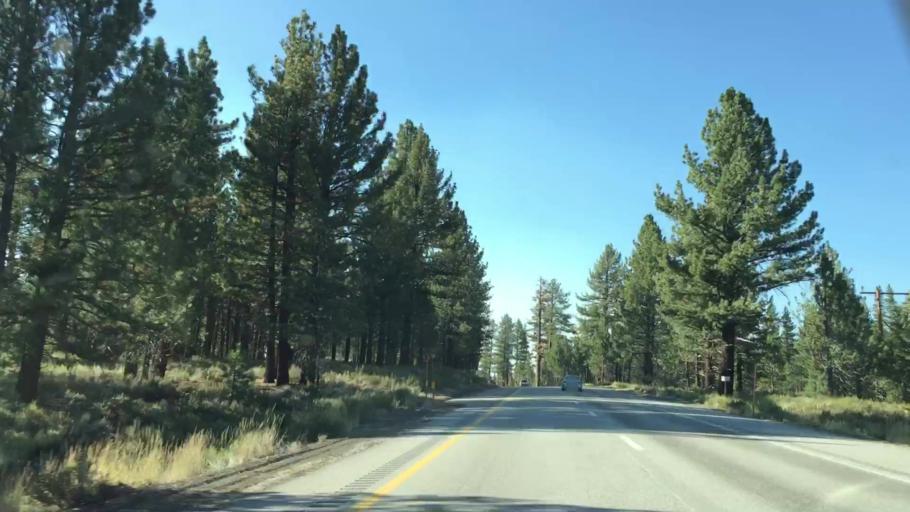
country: US
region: California
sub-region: Mono County
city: Mammoth Lakes
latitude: 37.7104
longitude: -118.9528
